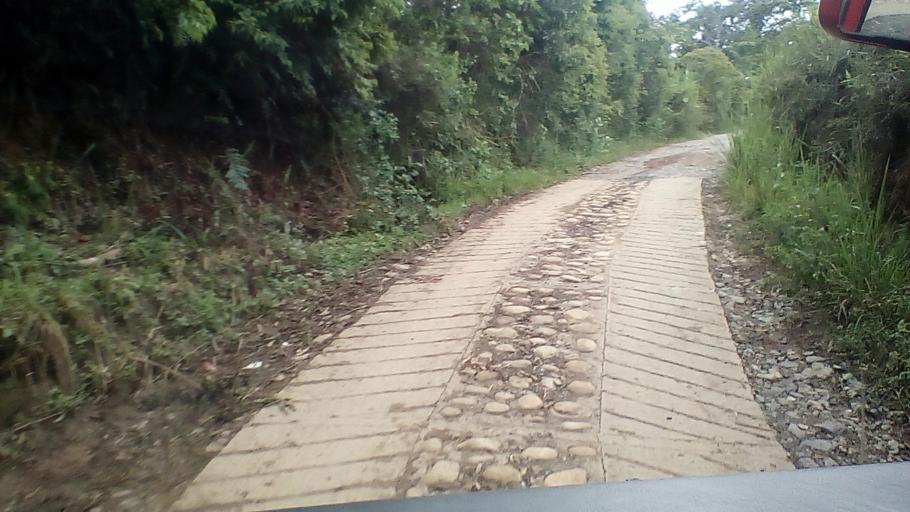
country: CO
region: Boyaca
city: Santana
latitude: 6.0265
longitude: -73.5171
